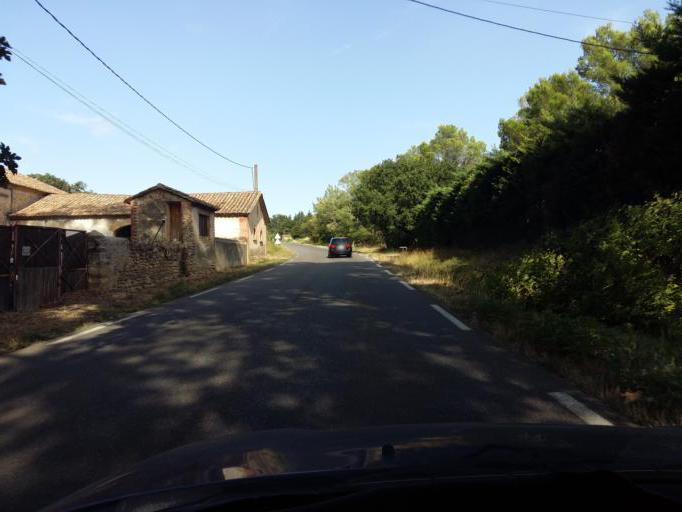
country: FR
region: Provence-Alpes-Cote d'Azur
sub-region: Departement du Vaucluse
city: Vacqueyras
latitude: 44.1249
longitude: 4.9812
